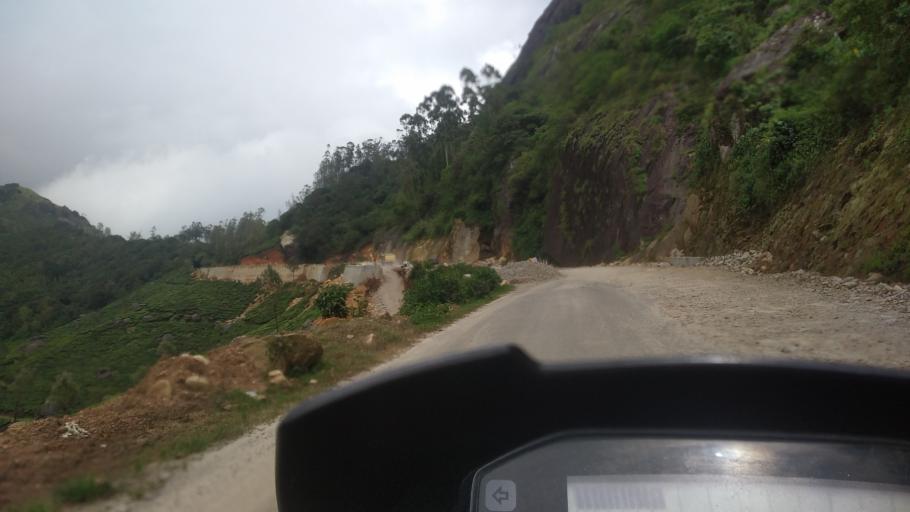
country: IN
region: Kerala
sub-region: Idukki
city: Munnar
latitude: 10.0364
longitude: 77.1171
